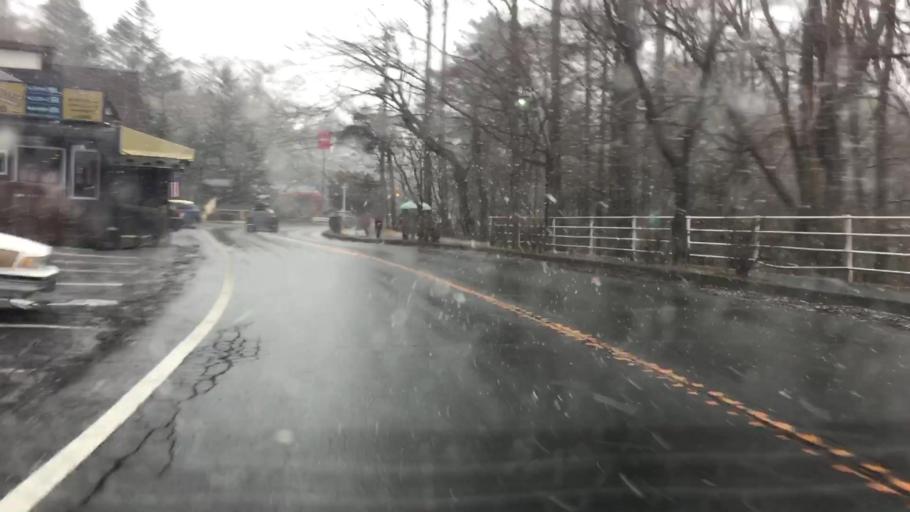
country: JP
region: Nagano
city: Komoro
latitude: 36.3601
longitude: 138.5895
